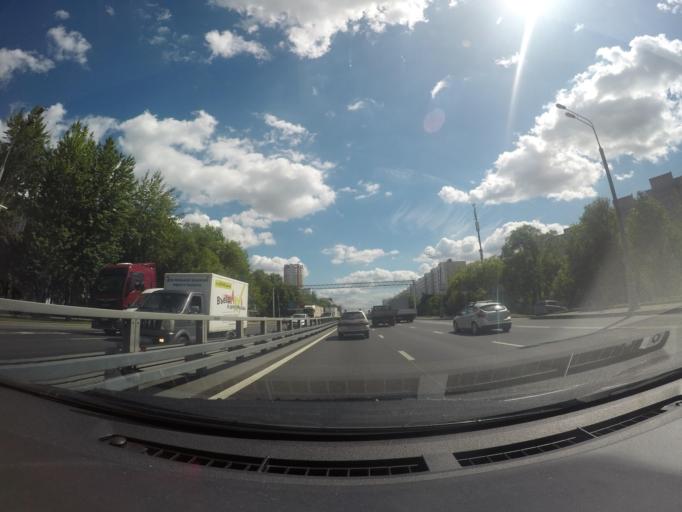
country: RU
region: Moscow
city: Kuz'minki
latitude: 55.7154
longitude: 37.8030
